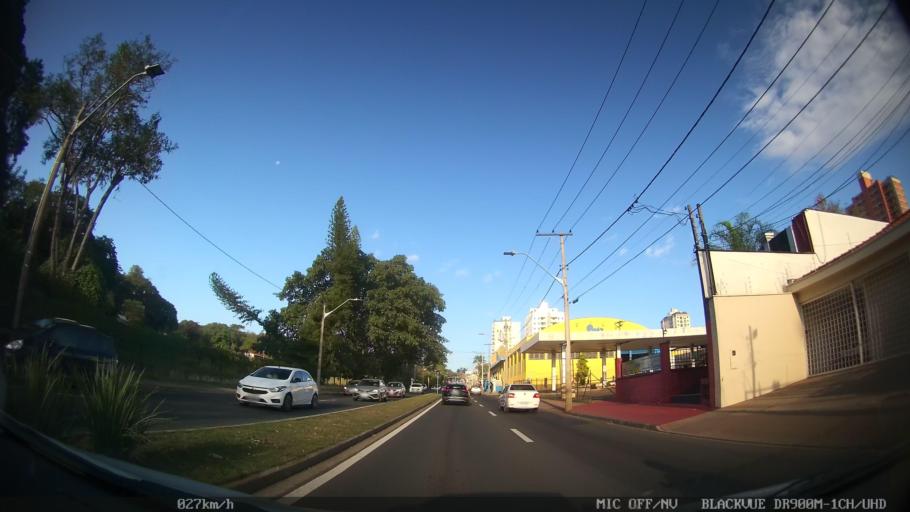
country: BR
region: Sao Paulo
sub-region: Piracicaba
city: Piracicaba
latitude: -22.7100
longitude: -47.6409
